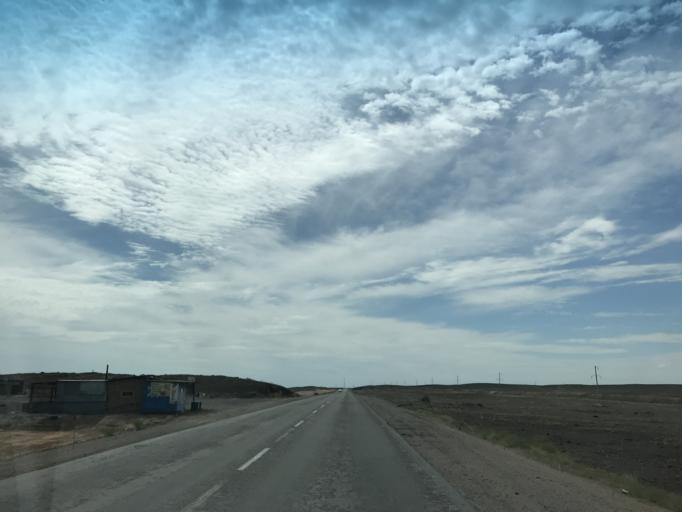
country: KZ
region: Almaty Oblysy
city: Ulken
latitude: 45.1855
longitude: 73.9198
